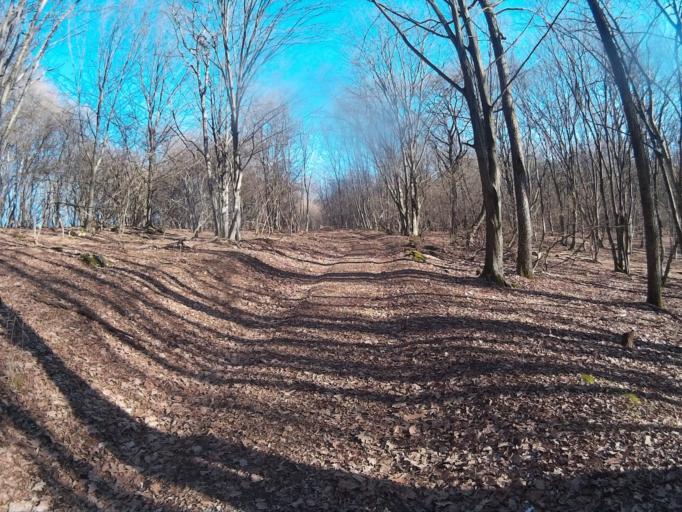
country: HU
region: Borsod-Abauj-Zemplen
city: Rudabanya
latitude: 48.5016
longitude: 20.5997
